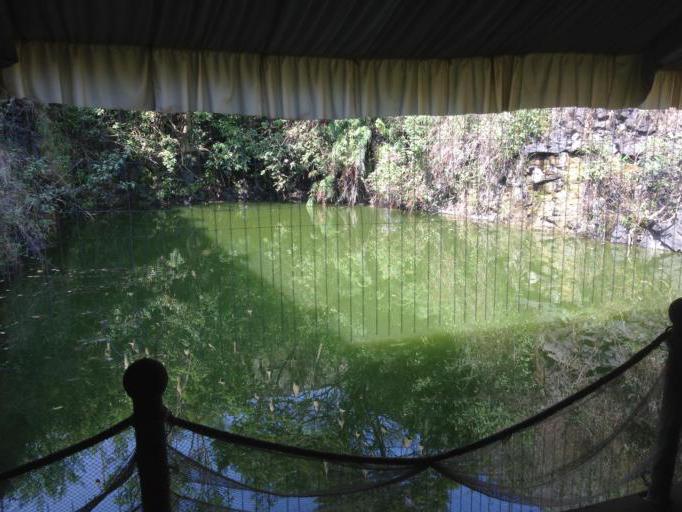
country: IN
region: Karnataka
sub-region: Belgaum
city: Belgaum
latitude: 15.8219
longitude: 74.4799
